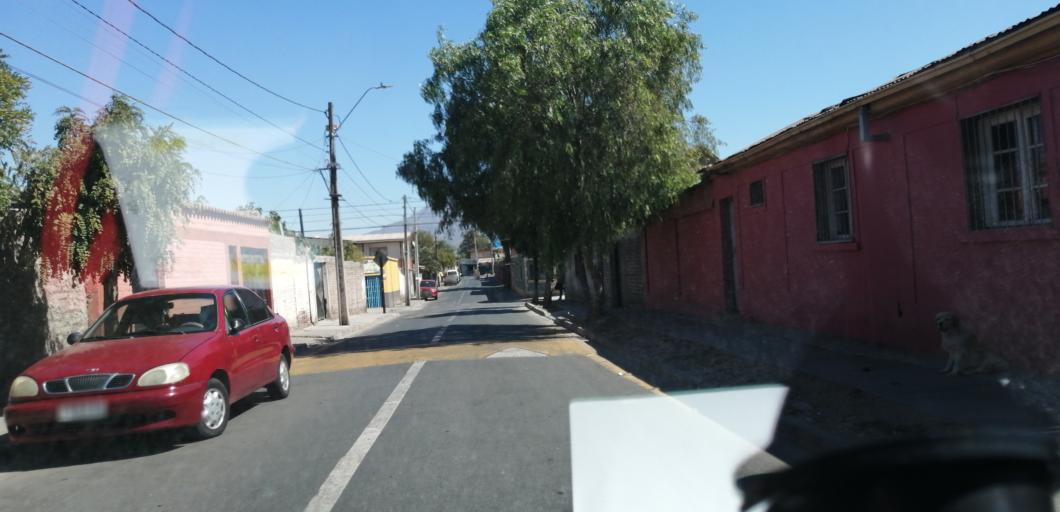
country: CL
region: Santiago Metropolitan
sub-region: Provincia de Santiago
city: Lo Prado
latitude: -33.4355
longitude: -70.7656
